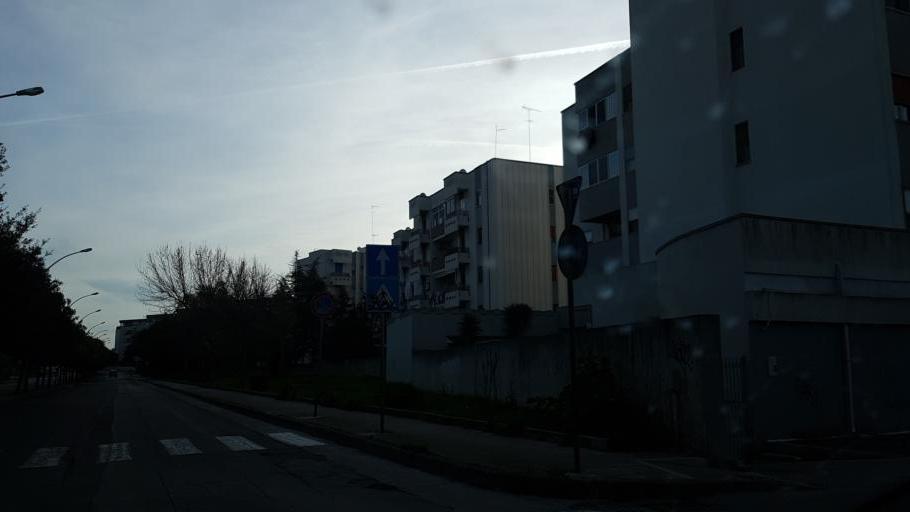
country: IT
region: Apulia
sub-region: Provincia di Brindisi
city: Brindisi
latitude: 40.6263
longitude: 17.9428
